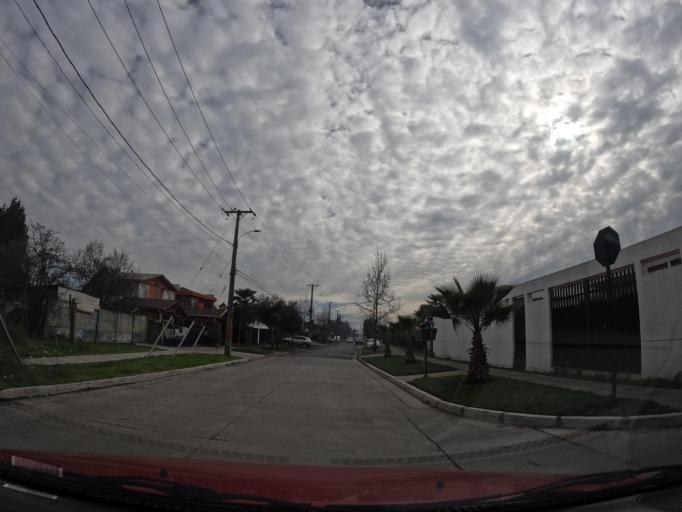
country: CL
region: Maule
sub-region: Provincia de Linares
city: Linares
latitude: -35.8341
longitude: -71.5994
